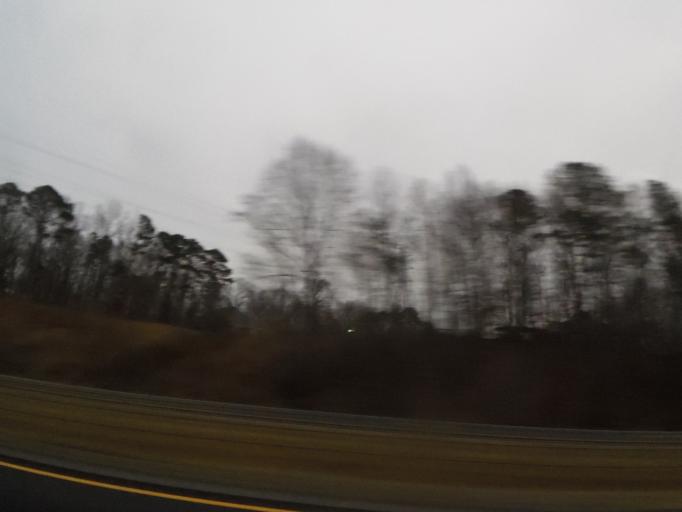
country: US
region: Alabama
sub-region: Cullman County
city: Cullman
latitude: 34.2197
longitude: -86.8760
